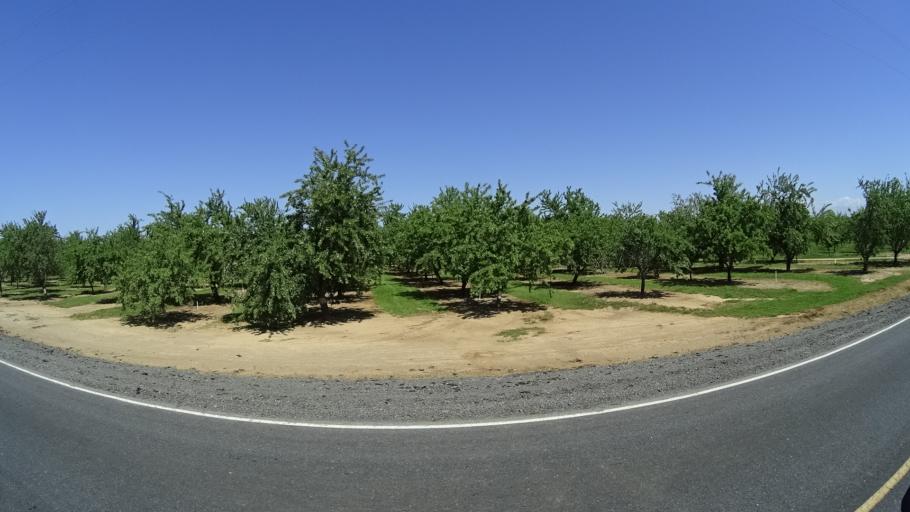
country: US
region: California
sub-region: Glenn County
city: Hamilton City
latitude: 39.7674
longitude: -122.1000
